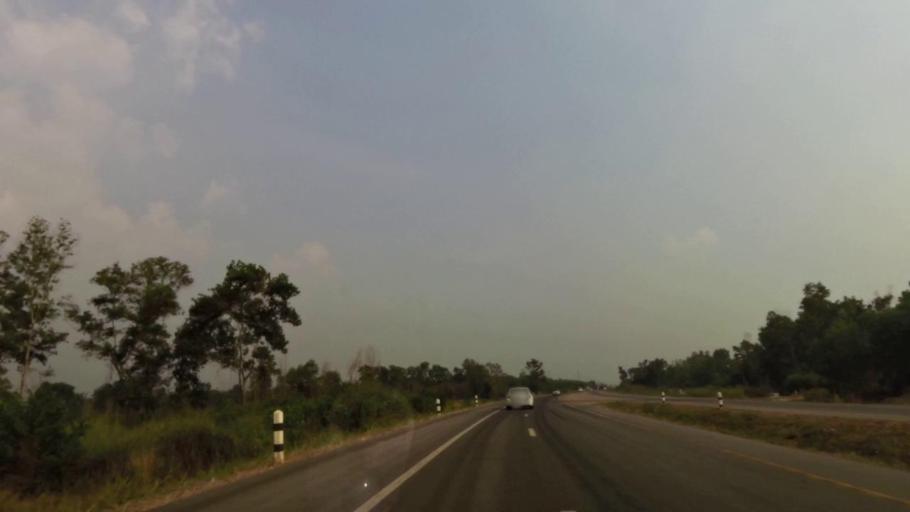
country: TH
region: Rayong
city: Klaeng
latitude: 12.8081
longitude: 101.6484
